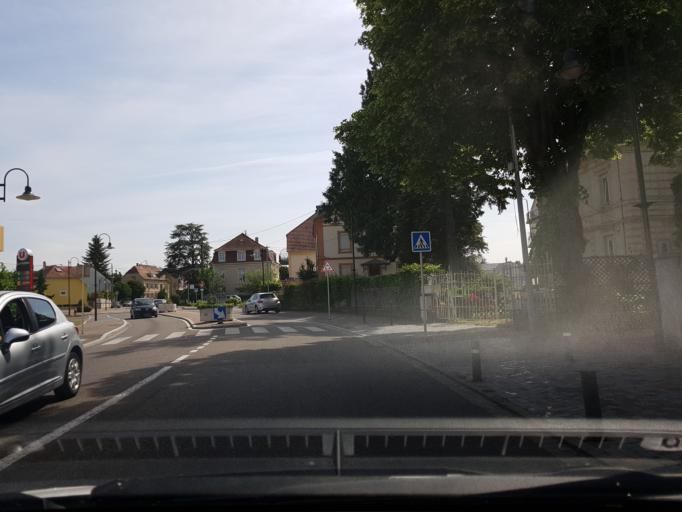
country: FR
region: Alsace
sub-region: Departement du Haut-Rhin
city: Brunstatt
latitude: 47.7248
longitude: 7.3197
